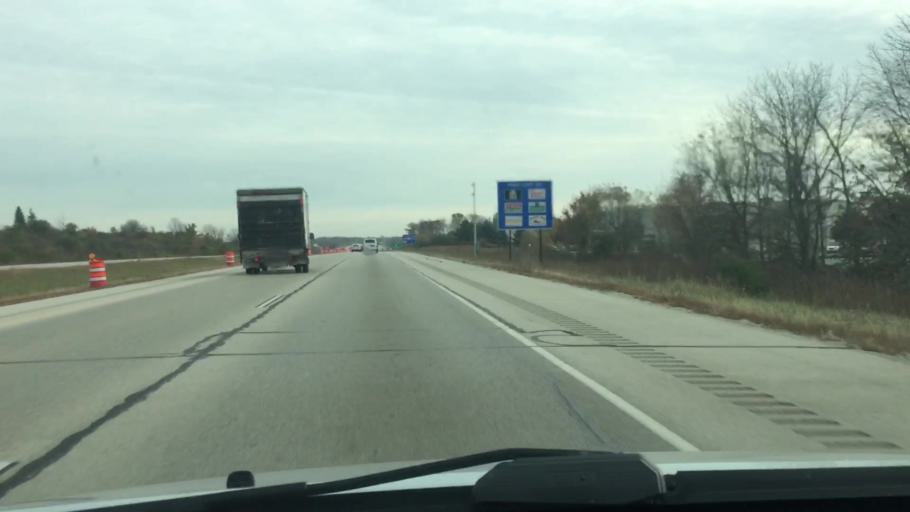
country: US
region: Wisconsin
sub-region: Waukesha County
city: New Berlin
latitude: 42.9446
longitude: -88.1212
